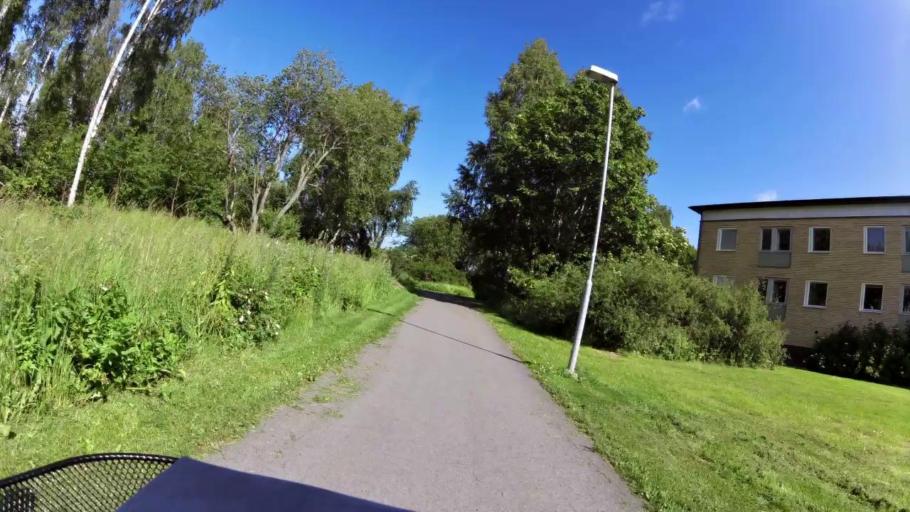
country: SE
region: OEstergoetland
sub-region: Linkopings Kommun
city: Linkoping
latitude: 58.3865
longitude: 15.6376
